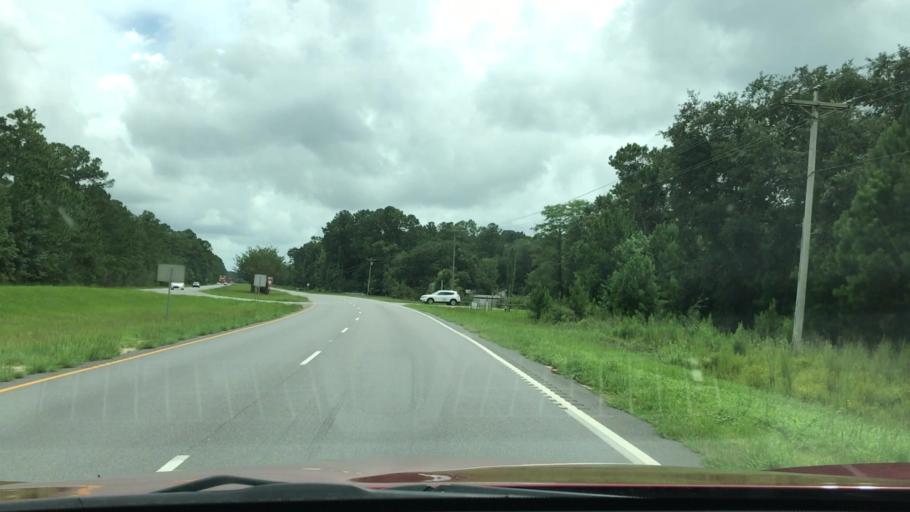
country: US
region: South Carolina
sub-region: Georgetown County
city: Georgetown
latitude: 33.2505
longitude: -79.3751
